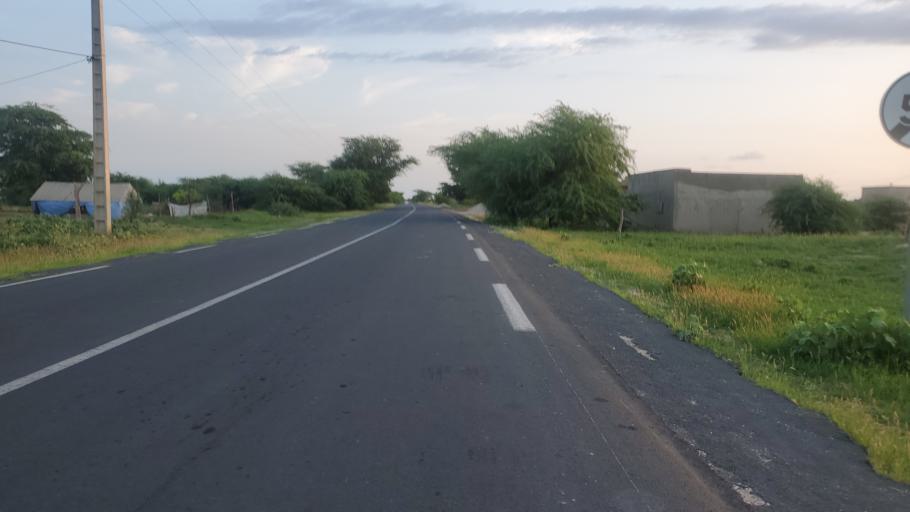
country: SN
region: Saint-Louis
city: Saint-Louis
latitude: 16.1343
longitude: -16.4118
